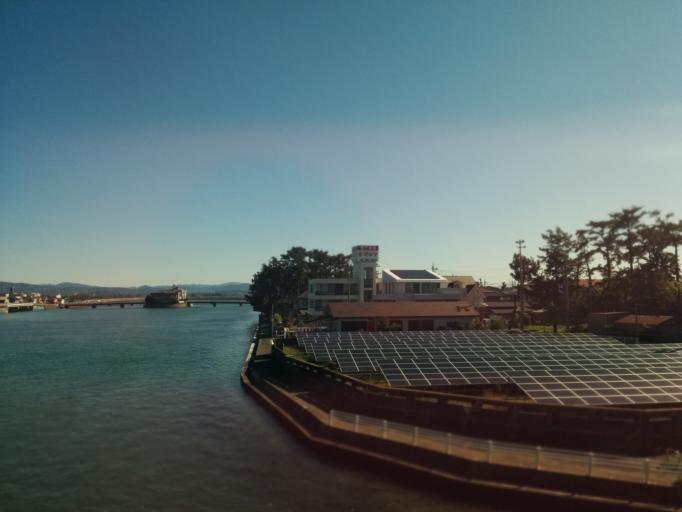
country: JP
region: Shizuoka
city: Kosai-shi
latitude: 34.6919
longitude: 137.5995
